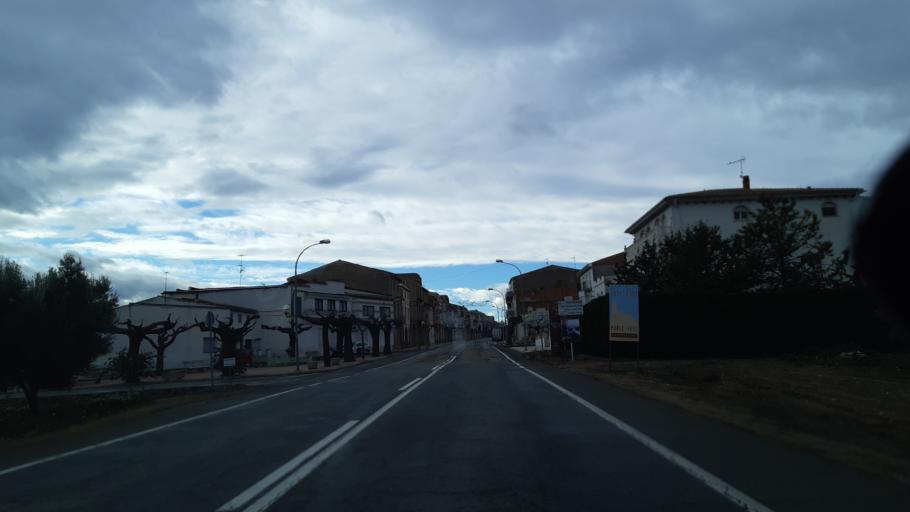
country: ES
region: Catalonia
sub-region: Provincia de Tarragona
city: Gandesa
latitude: 41.0789
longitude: 0.4816
